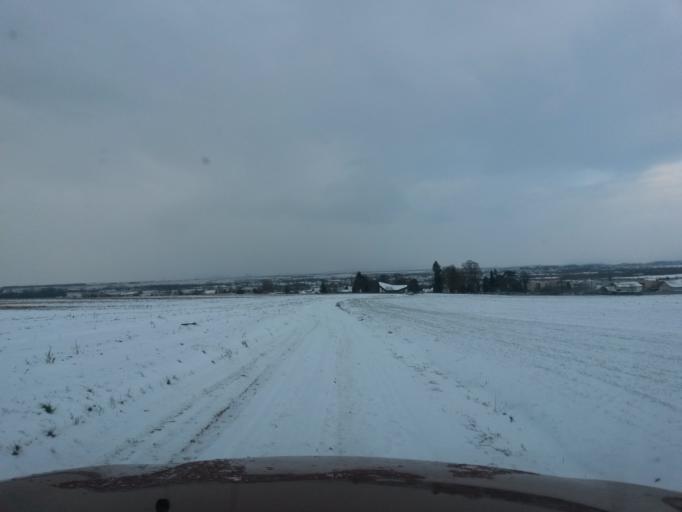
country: SK
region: Kosicky
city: Kosice
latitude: 48.6019
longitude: 21.3578
